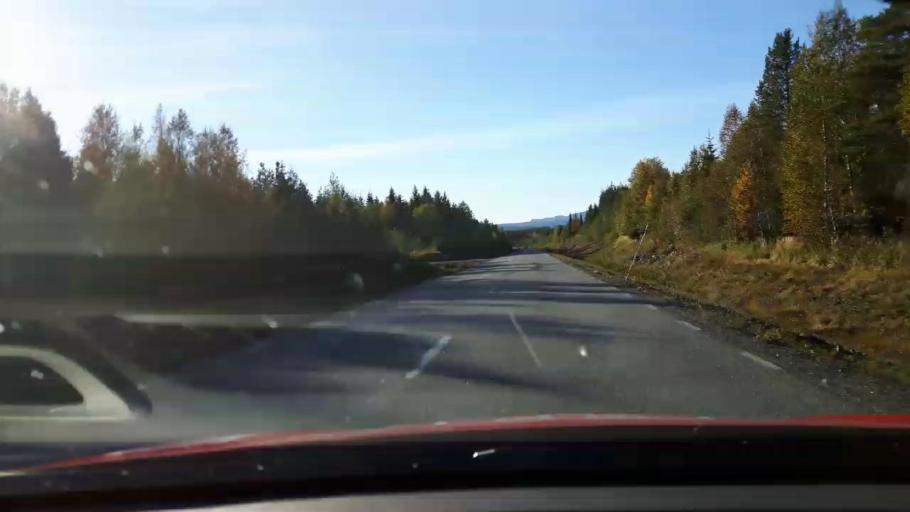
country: SE
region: Jaemtland
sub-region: OEstersunds Kommun
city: Lit
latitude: 63.8589
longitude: 14.9809
